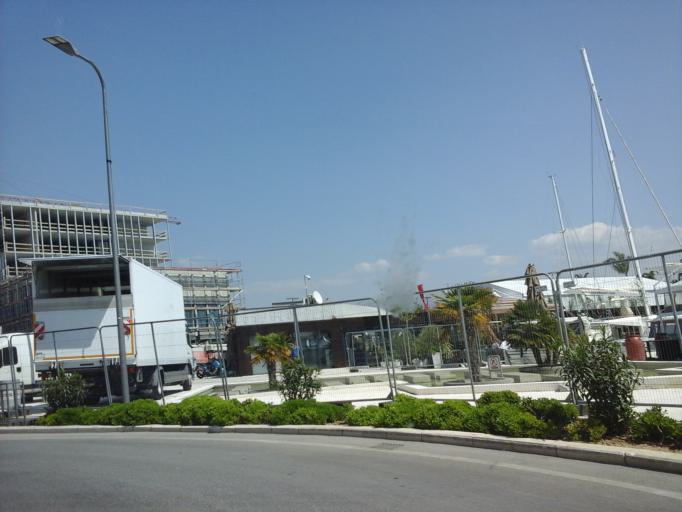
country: HR
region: Splitsko-Dalmatinska
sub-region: Grad Split
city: Split
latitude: 43.5060
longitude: 16.4321
